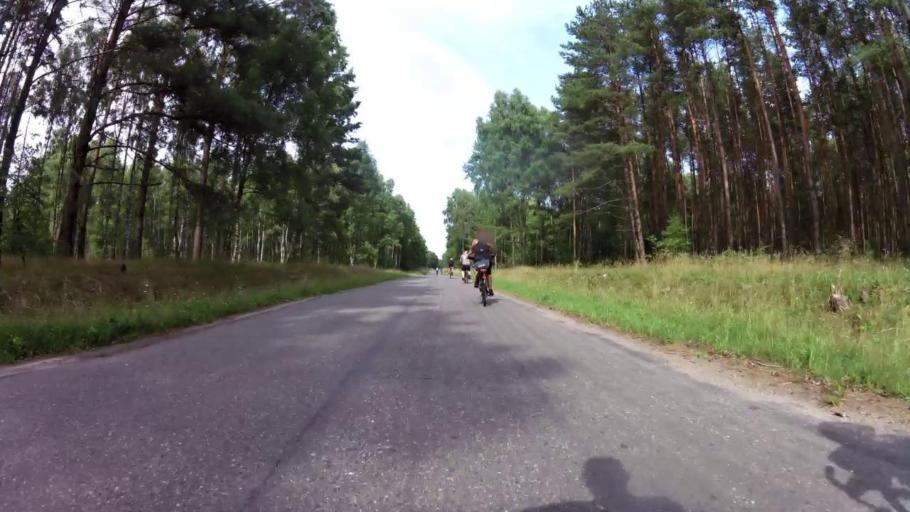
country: PL
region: West Pomeranian Voivodeship
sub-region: Powiat stargardzki
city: Insko
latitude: 53.4212
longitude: 15.6089
